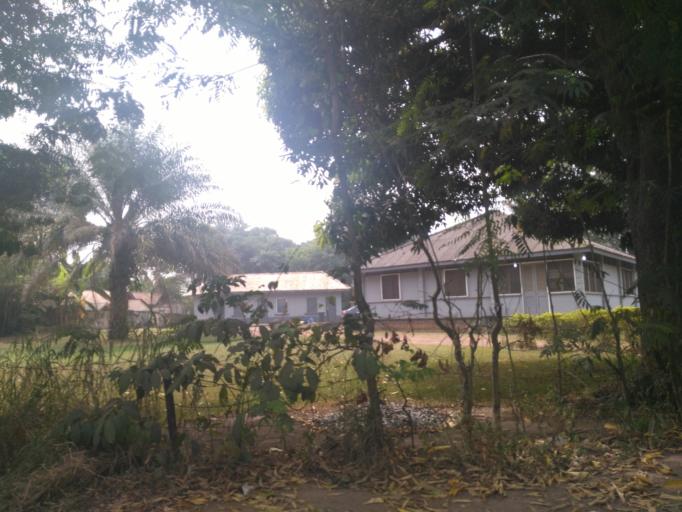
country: GH
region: Ashanti
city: Kumasi
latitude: 6.6869
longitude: -1.6305
